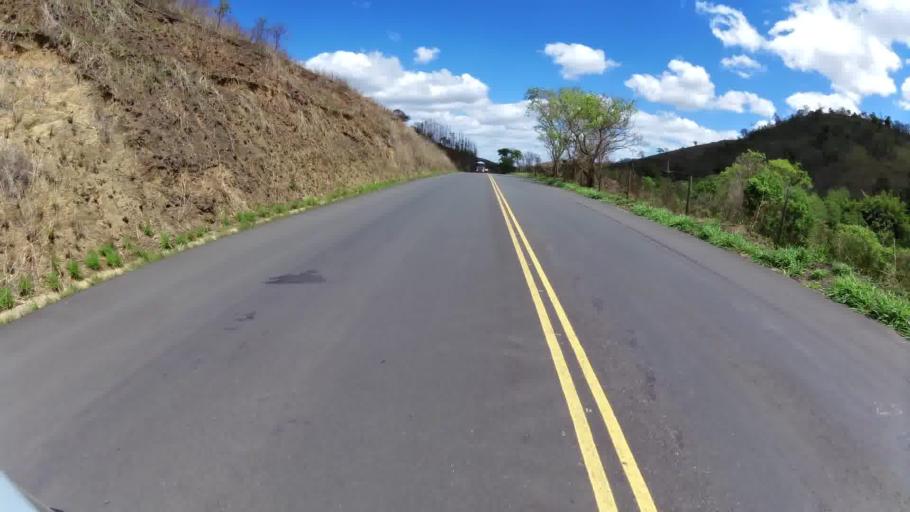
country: BR
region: Rio de Janeiro
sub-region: Itaperuna
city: Itaperuna
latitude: -21.3384
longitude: -41.8941
